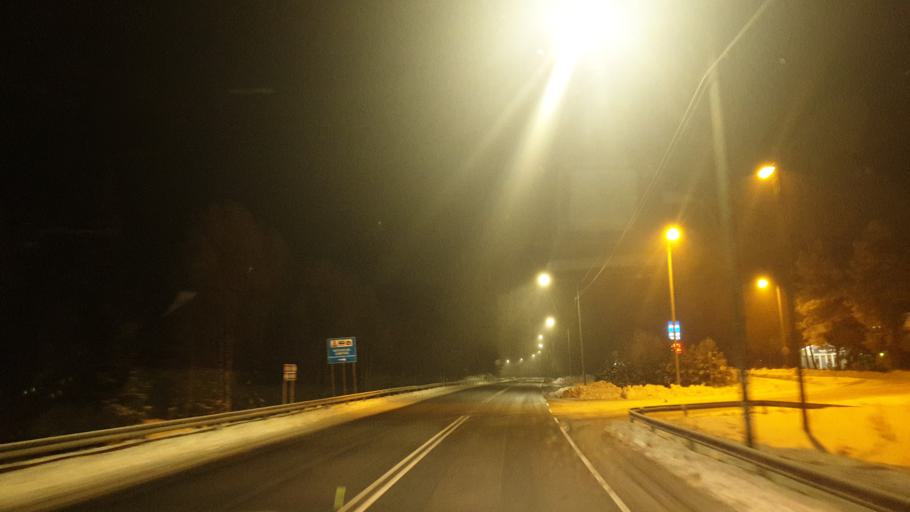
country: FI
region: Northern Ostrobothnia
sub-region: Oulunkaari
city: Kuivaniemi
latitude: 65.5281
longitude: 25.2585
